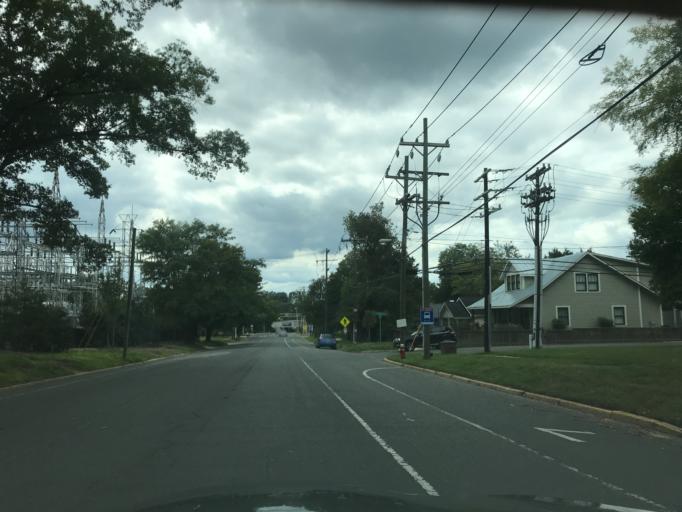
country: US
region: North Carolina
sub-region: Orange County
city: Chapel Hill
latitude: 35.9080
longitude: -79.0613
